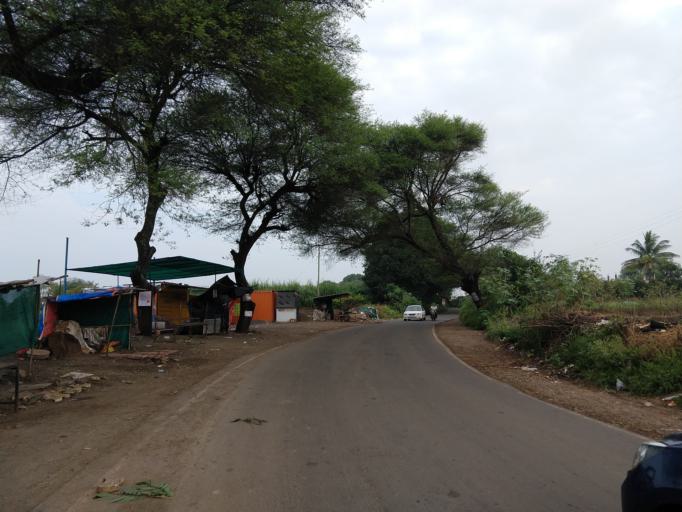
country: IN
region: Maharashtra
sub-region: Pune Division
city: Sasvad
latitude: 18.3602
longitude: 73.9955
